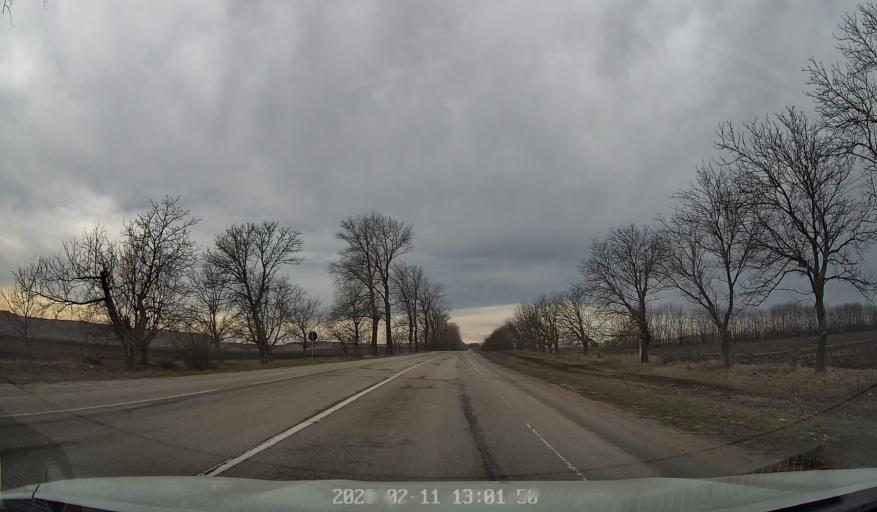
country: MD
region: Briceni
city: Briceni
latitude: 48.3162
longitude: 26.9940
